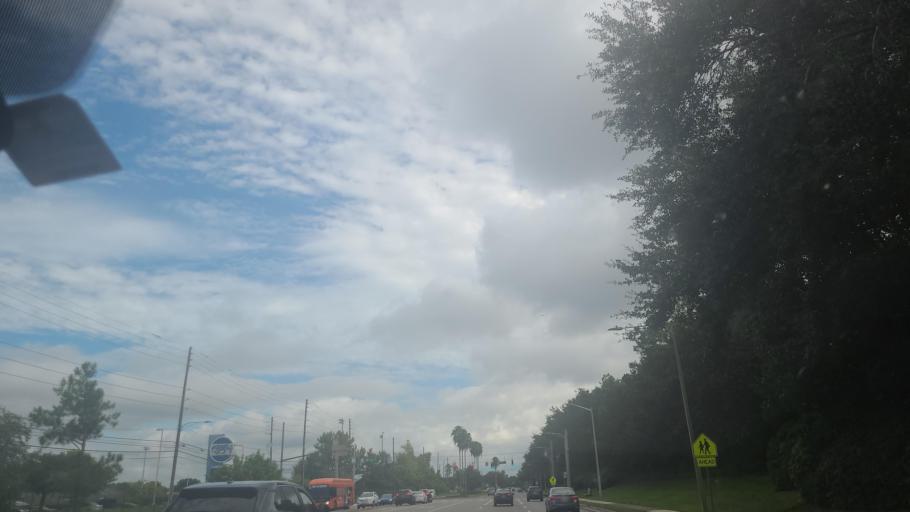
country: US
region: Florida
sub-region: Orange County
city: Doctor Phillips
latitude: 28.4705
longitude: -81.4749
